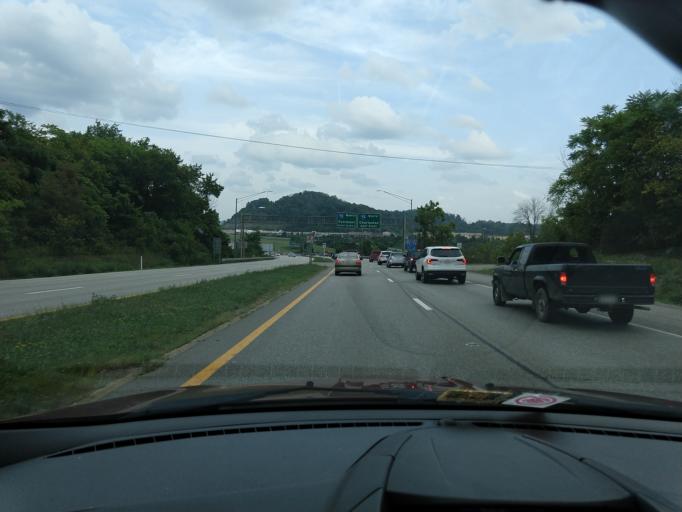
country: US
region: West Virginia
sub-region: Harrison County
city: Despard
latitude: 39.2777
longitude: -80.2908
